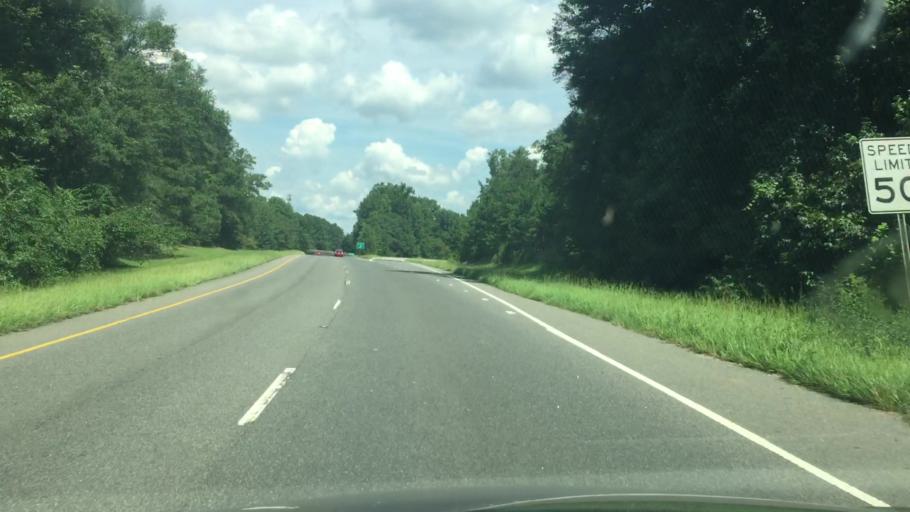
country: US
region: North Carolina
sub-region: Richmond County
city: Rockingham
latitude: 34.9275
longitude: -79.7798
